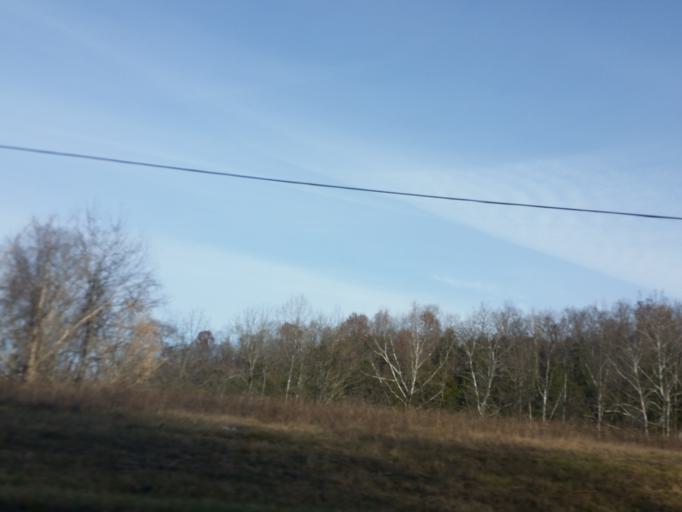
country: US
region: Kentucky
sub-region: Harrison County
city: Cynthiana
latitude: 38.5362
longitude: -84.2814
